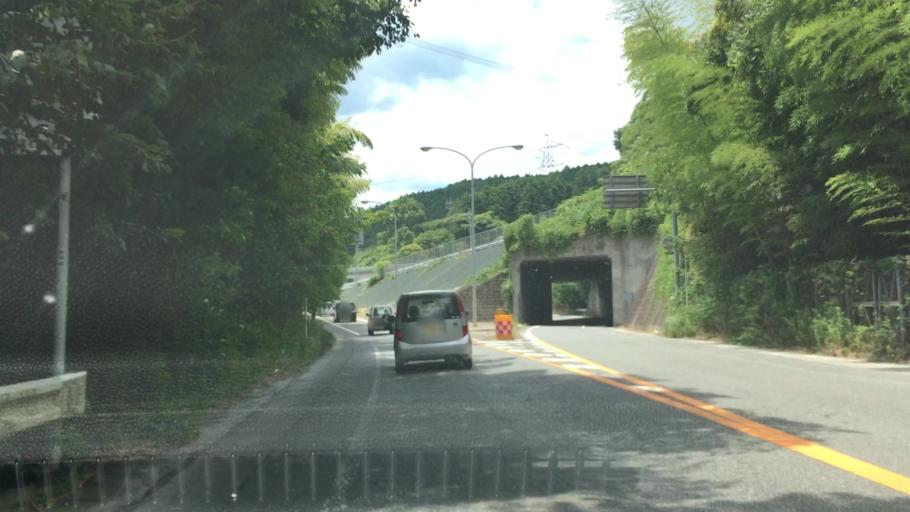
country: JP
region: Fukuoka
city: Chikushino-shi
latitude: 33.4433
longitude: 130.5295
